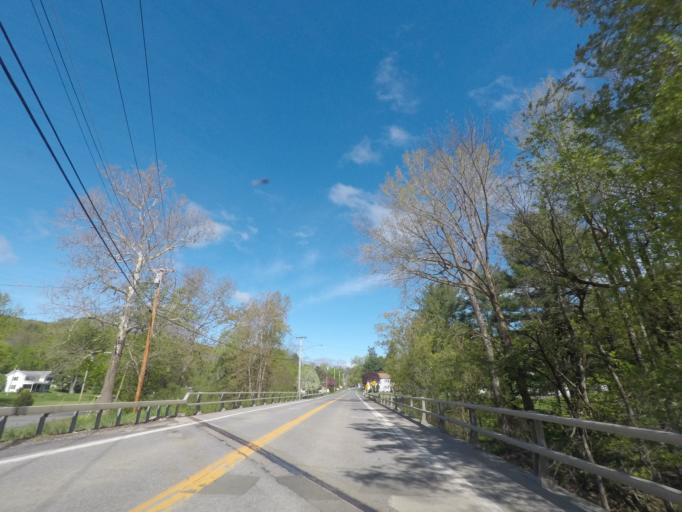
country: US
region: New York
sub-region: Albany County
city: Ravena
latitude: 42.4699
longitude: -73.8916
